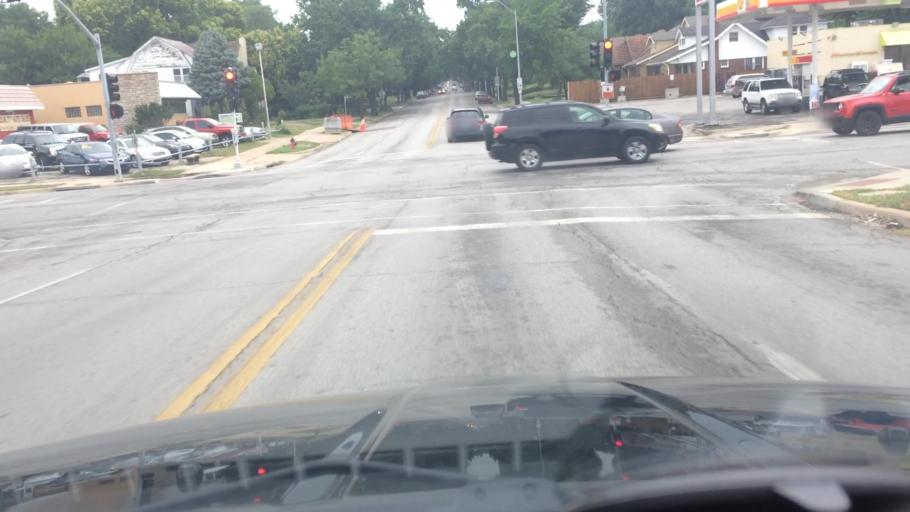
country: US
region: Kansas
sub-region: Johnson County
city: Mission Hills
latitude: 39.0131
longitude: -94.5769
